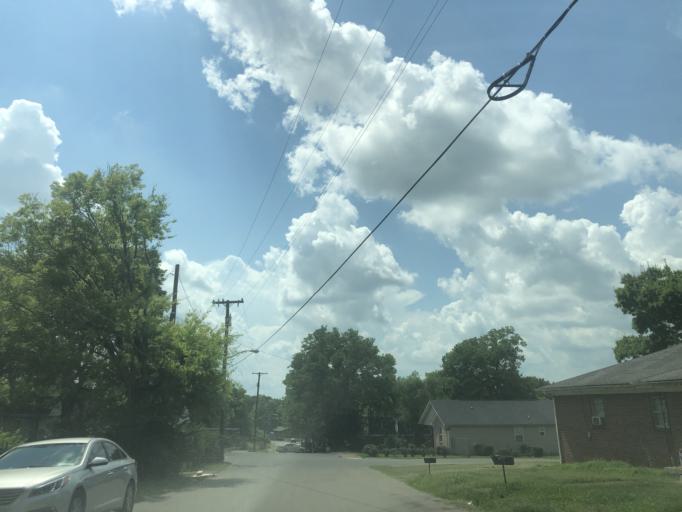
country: US
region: Tennessee
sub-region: Davidson County
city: Nashville
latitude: 36.1605
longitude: -86.8115
